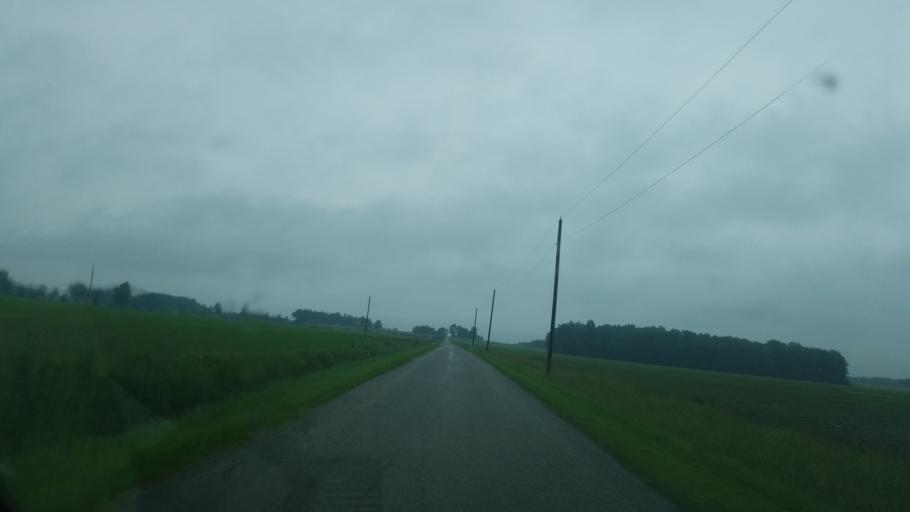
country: US
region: Ohio
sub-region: Huron County
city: Willard
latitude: 40.9330
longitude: -82.7975
